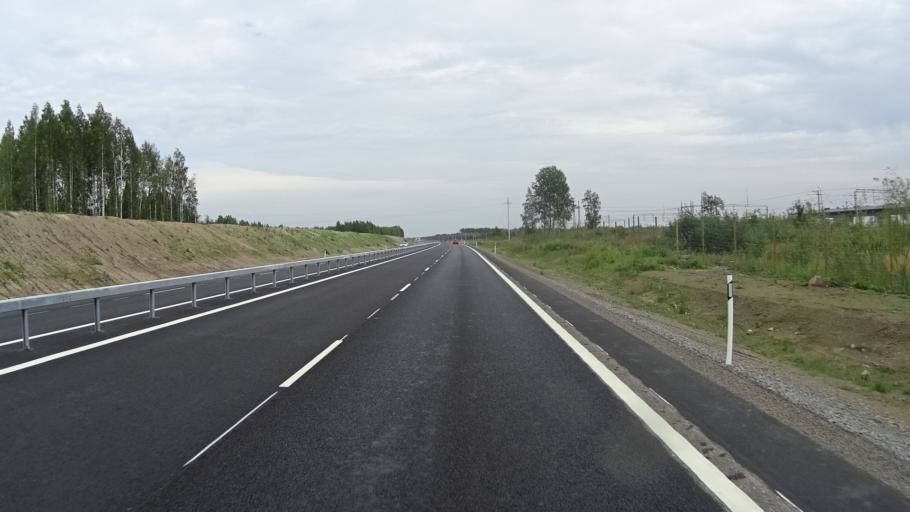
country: FI
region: South Karelia
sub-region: Lappeenranta
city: Lemi
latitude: 60.9452
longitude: 27.7608
